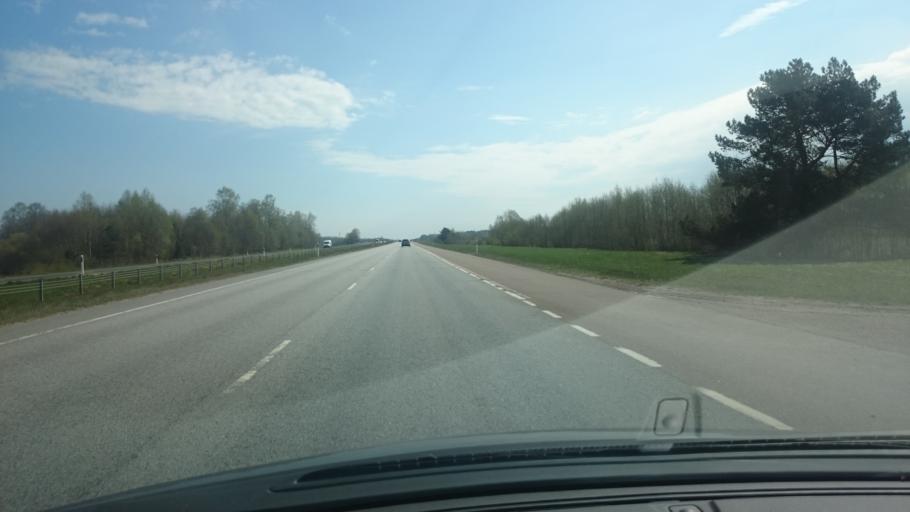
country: EE
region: Harju
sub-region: Anija vald
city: Kehra
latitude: 59.4406
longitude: 25.2951
